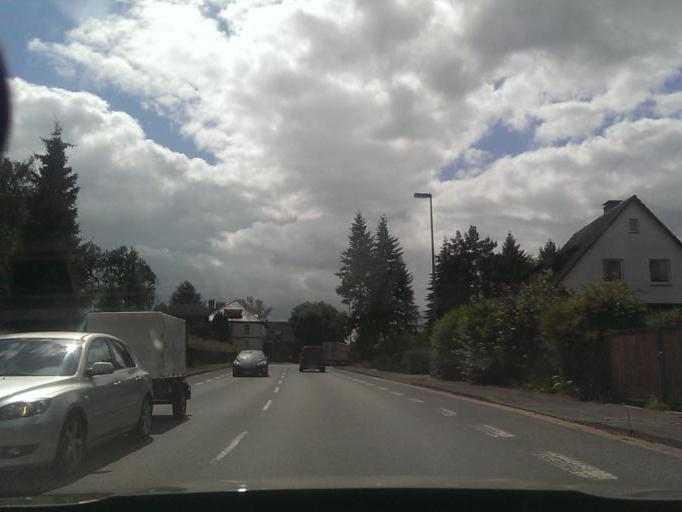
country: DE
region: Lower Saxony
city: Negenborn
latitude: 51.8912
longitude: 9.5717
